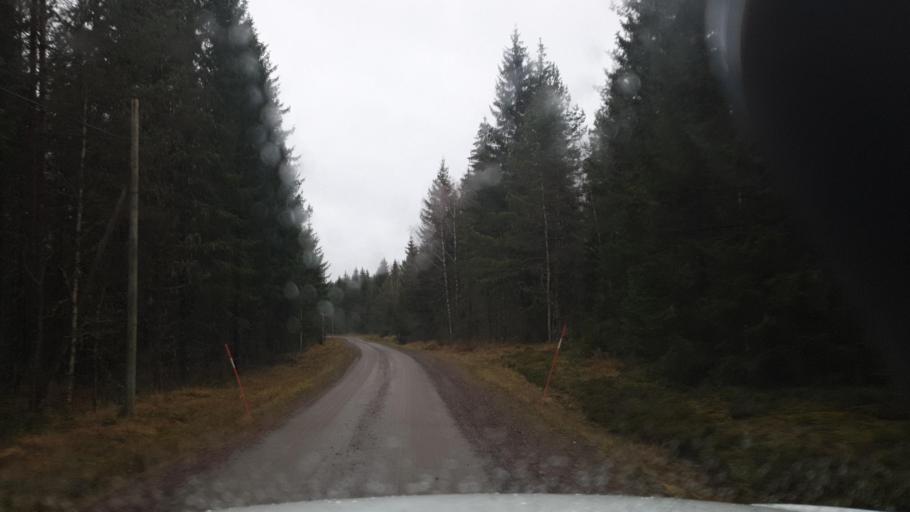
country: SE
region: Vaermland
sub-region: Eda Kommun
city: Charlottenberg
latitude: 59.9041
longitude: 12.3809
